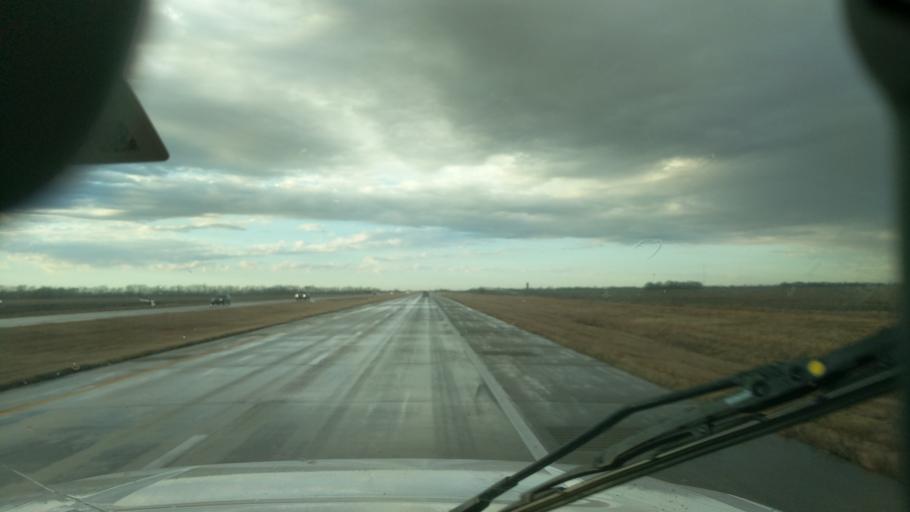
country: US
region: Kansas
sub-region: Harvey County
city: North Newton
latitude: 38.0909
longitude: -97.3587
